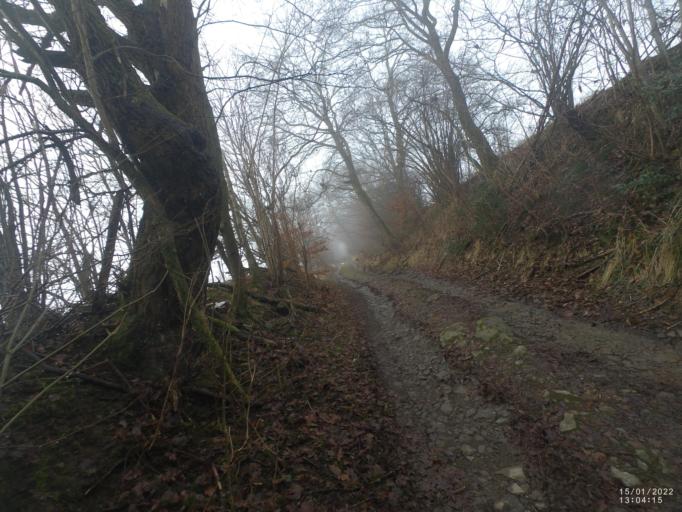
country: DE
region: North Rhine-Westphalia
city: Kierspe
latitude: 51.1117
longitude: 7.6022
